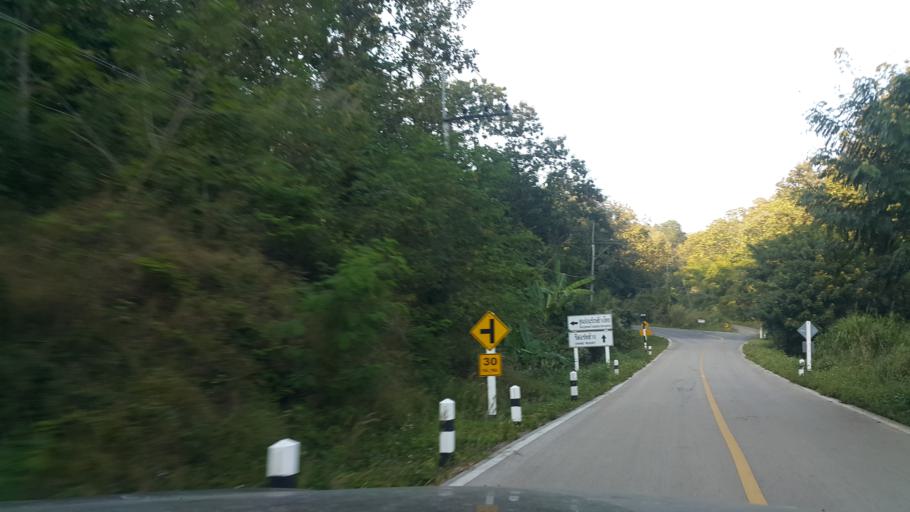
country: TH
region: Lampang
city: Hang Chat
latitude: 18.3477
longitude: 99.2525
